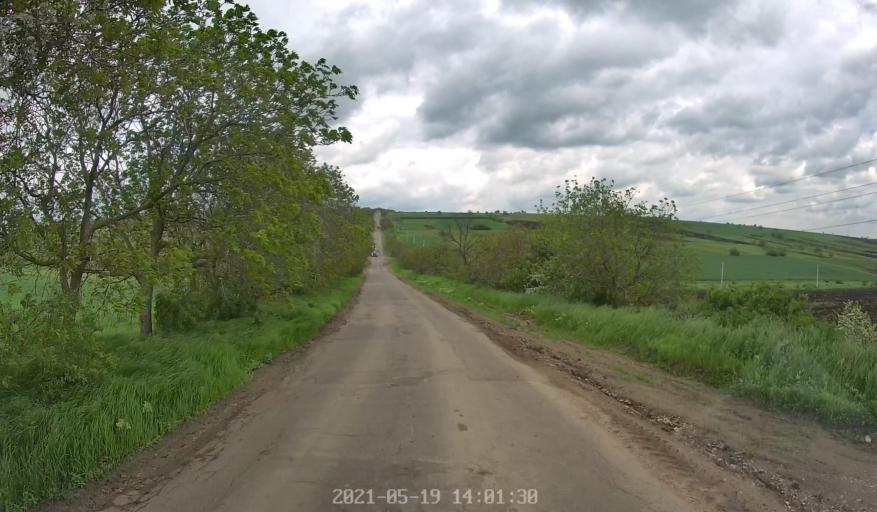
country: MD
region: Chisinau
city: Chisinau
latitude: 47.0320
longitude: 28.9381
